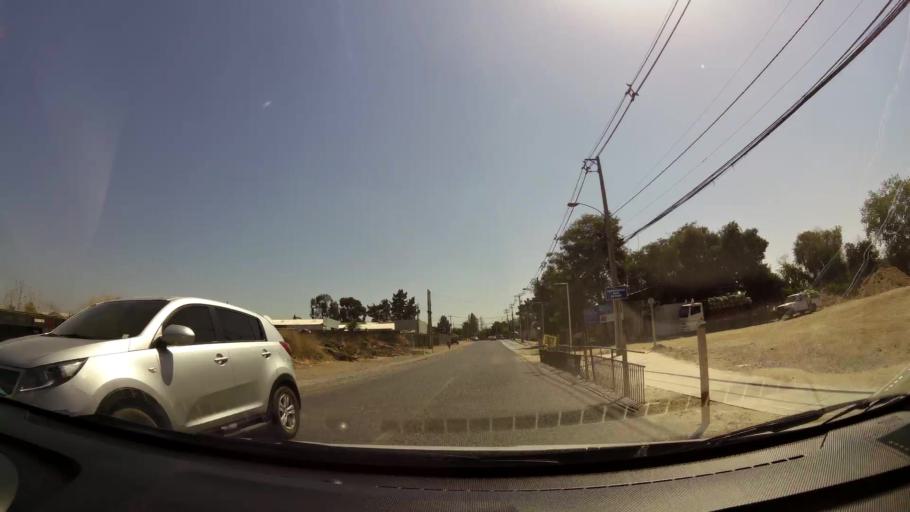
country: CL
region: Maule
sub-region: Provincia de Talca
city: Talca
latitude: -35.4250
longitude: -71.6379
